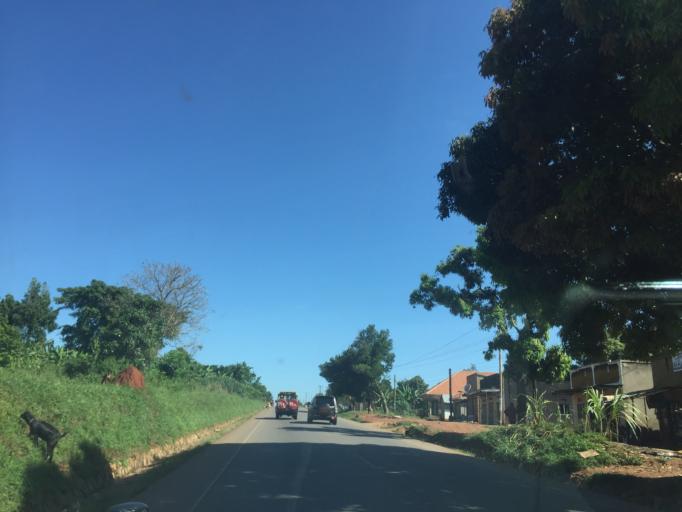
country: UG
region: Central Region
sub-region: Luwero District
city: Wobulenzi
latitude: 0.7465
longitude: 32.5161
